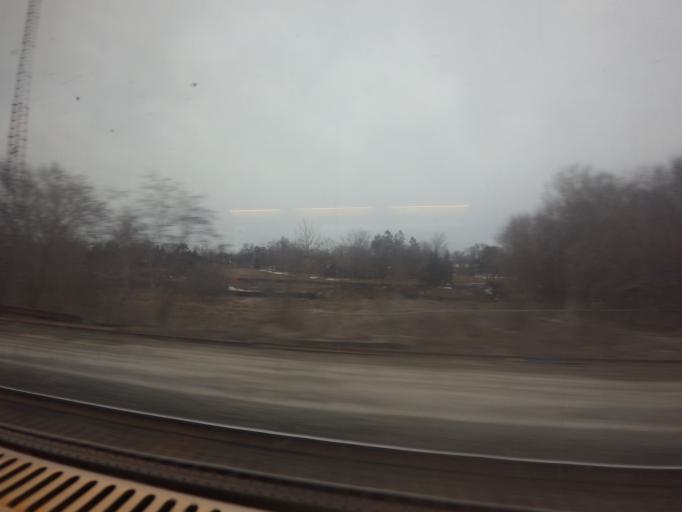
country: CA
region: Ontario
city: Scarborough
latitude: 43.7132
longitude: -79.2578
